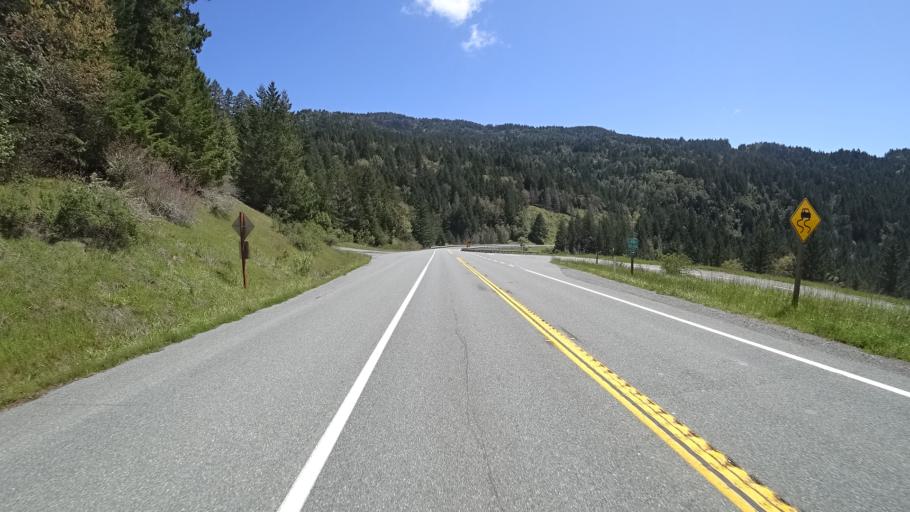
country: US
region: California
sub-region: Humboldt County
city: Willow Creek
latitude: 40.9230
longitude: -123.7979
